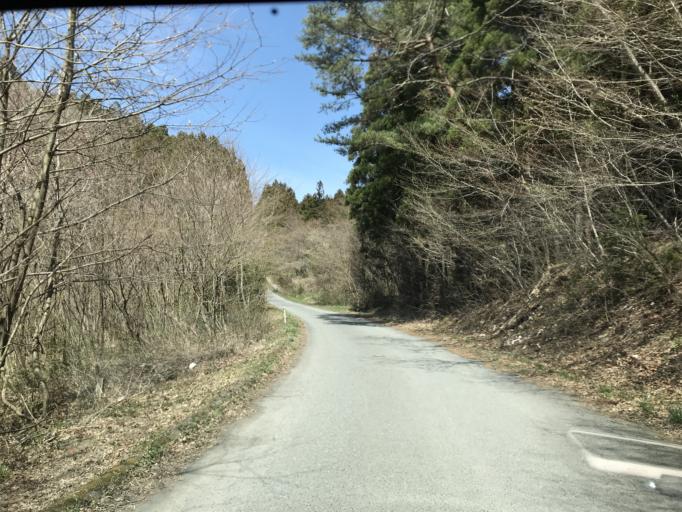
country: JP
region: Iwate
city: Ichinoseki
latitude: 38.8152
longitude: 141.2806
